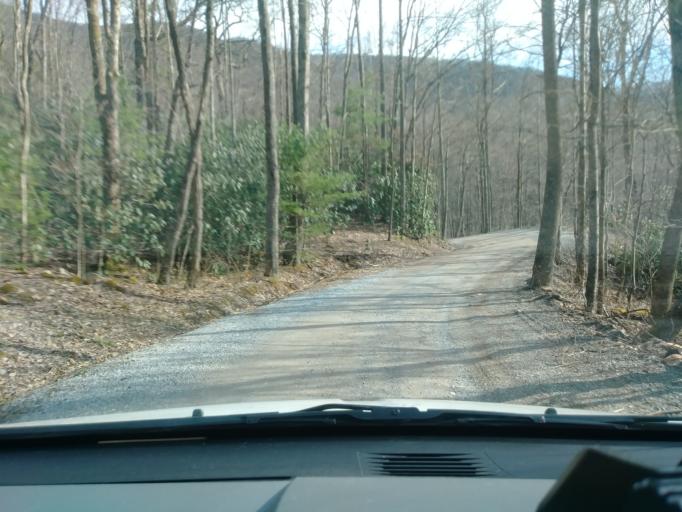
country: US
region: Tennessee
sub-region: Greene County
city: Tusculum
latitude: 36.0270
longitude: -82.7282
